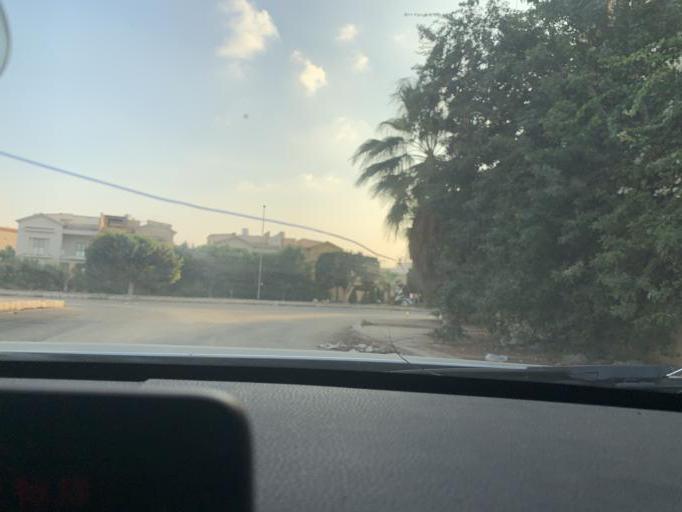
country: EG
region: Muhafazat al Qalyubiyah
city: Al Khankah
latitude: 30.0169
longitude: 31.4807
